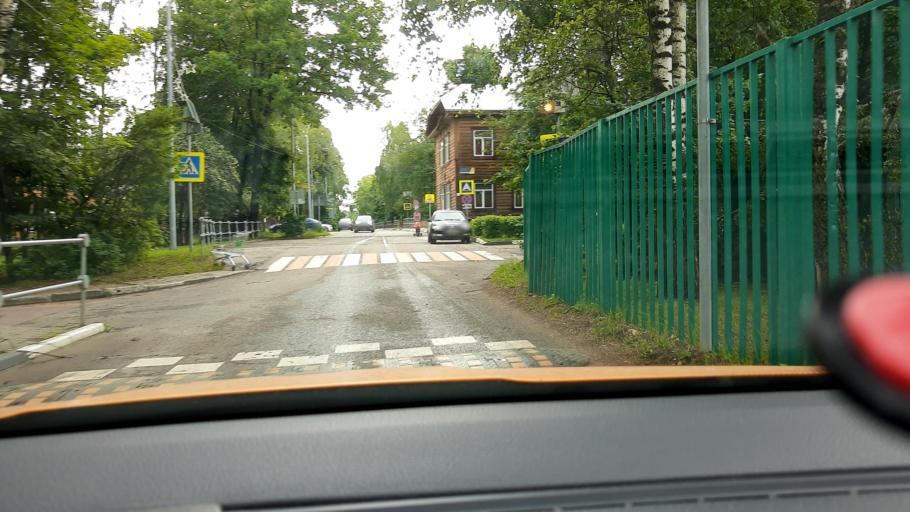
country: RU
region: Moskovskaya
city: Gorki Vtoryye
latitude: 55.7256
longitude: 37.1608
